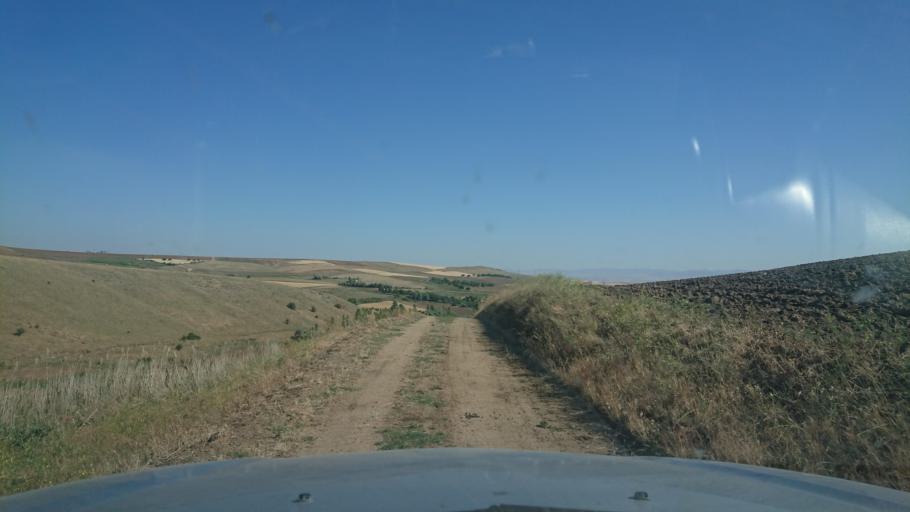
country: TR
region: Aksaray
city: Agacoren
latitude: 38.8372
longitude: 33.9267
